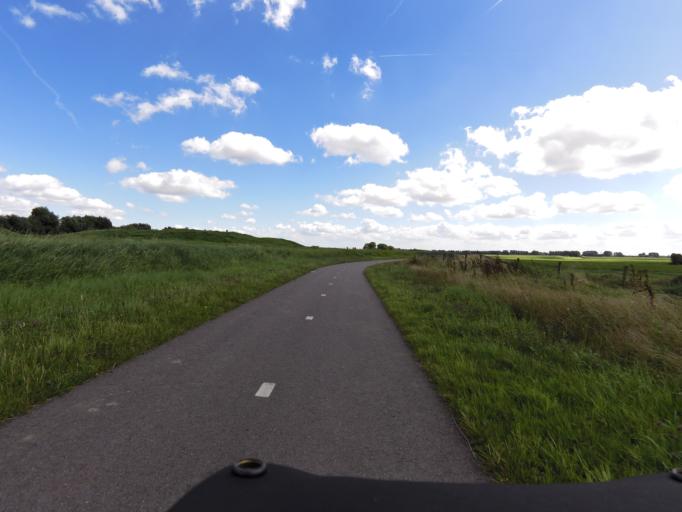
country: NL
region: South Holland
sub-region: Gemeente Oud-Beijerland
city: Oud-Beijerland
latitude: 51.8388
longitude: 4.3761
